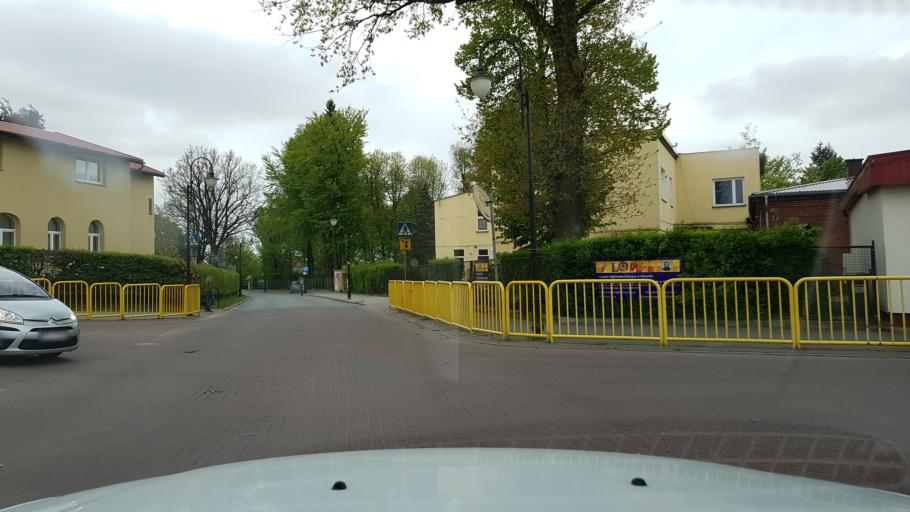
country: PL
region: West Pomeranian Voivodeship
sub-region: Powiat slawienski
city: Slawno
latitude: 54.3700
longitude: 16.6794
